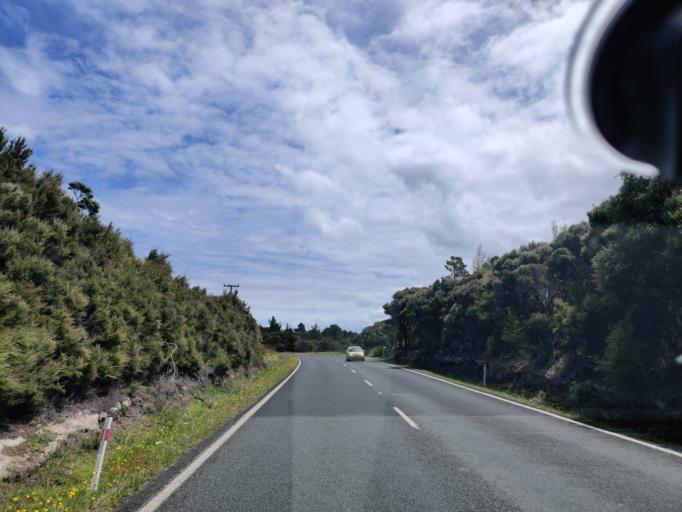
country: NZ
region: Northland
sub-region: Far North District
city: Kaitaia
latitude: -34.6646
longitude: 172.9728
